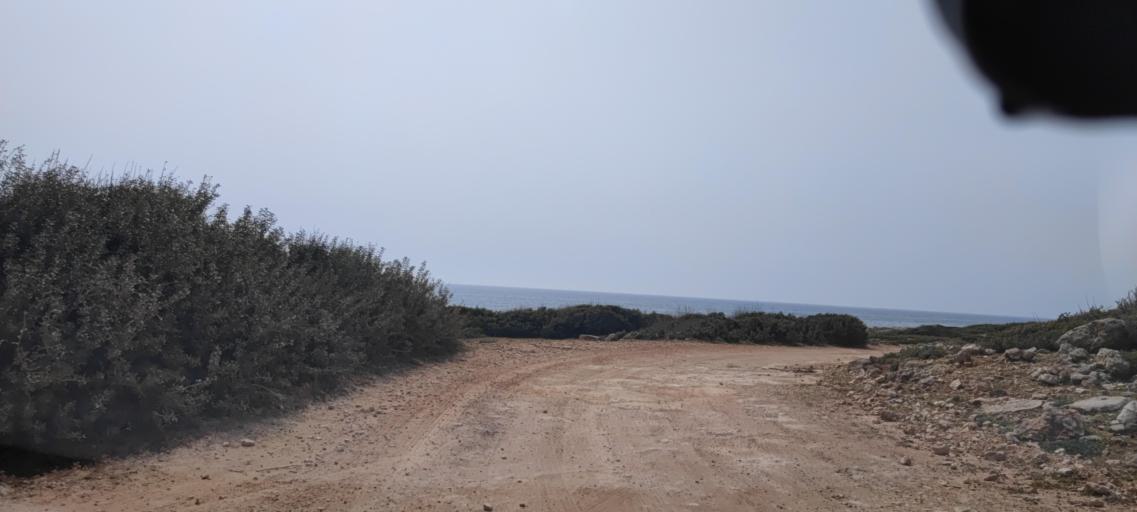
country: CY
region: Ammochostos
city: Rizokarpaso
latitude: 35.6783
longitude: 34.5777
